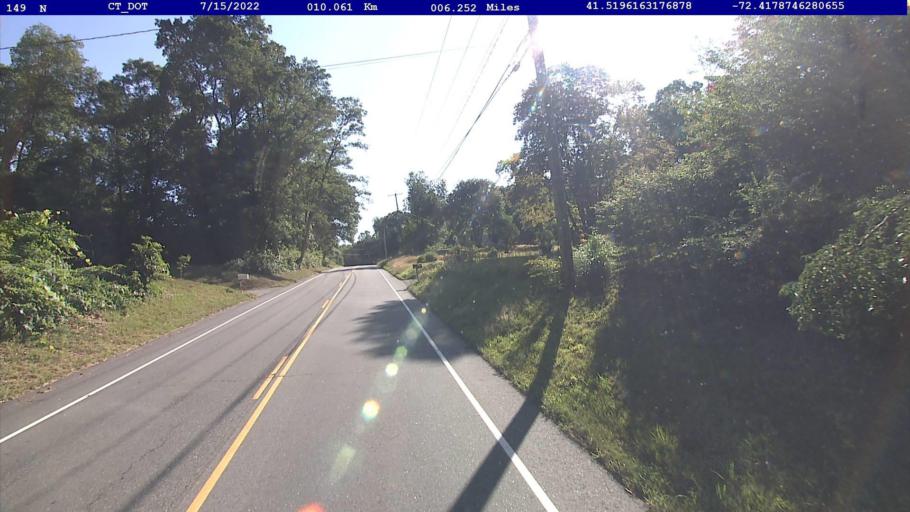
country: US
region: Connecticut
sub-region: Middlesex County
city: Moodus
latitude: 41.5196
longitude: -72.4177
